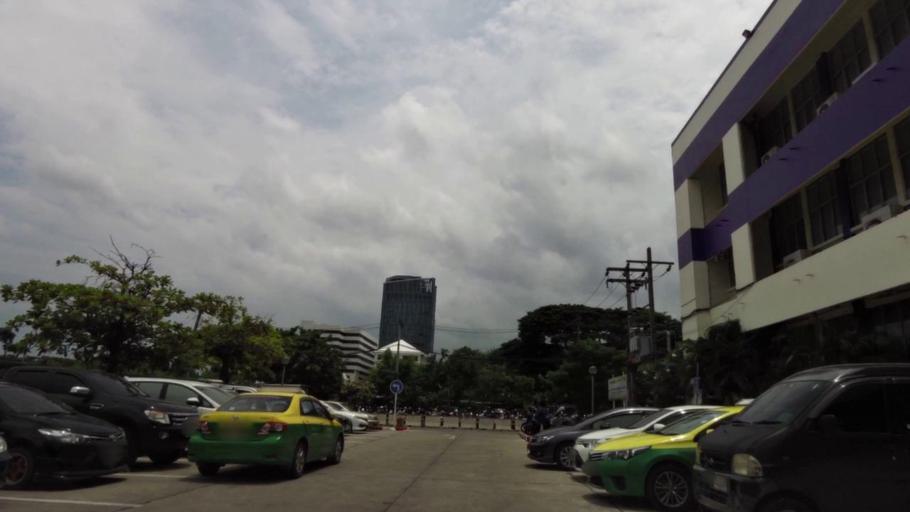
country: TH
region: Bangkok
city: Phra Khanong
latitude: 13.6965
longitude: 100.6093
